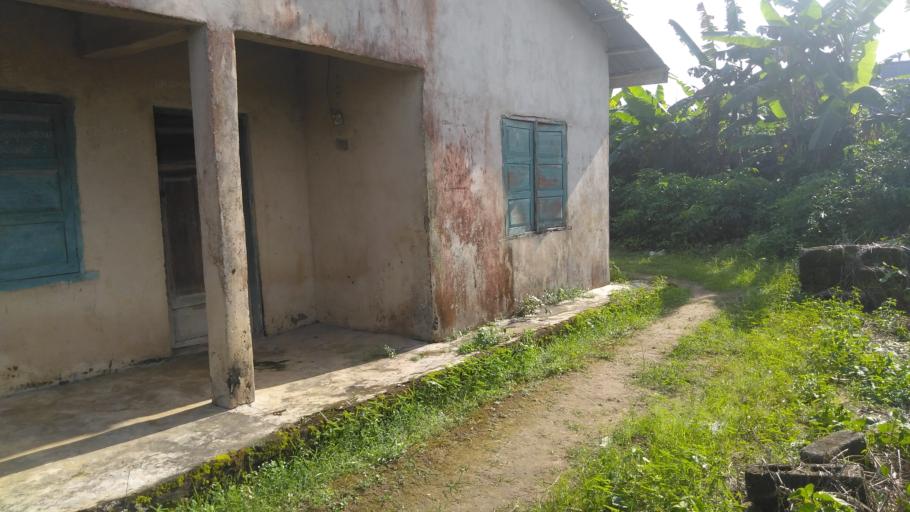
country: NG
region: Edo
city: Siluko
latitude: 6.1424
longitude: 5.2005
